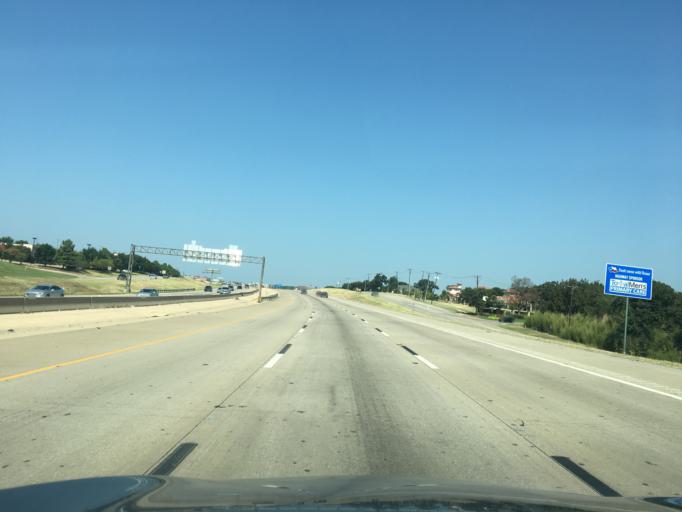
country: US
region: Texas
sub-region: Tarrant County
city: Southlake
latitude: 32.9427
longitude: -97.1063
